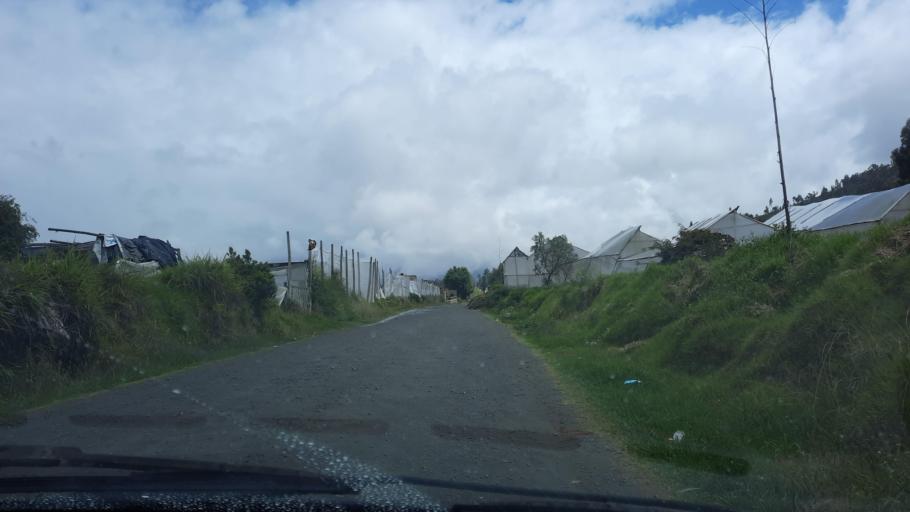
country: EC
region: Chimborazo
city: Riobamba
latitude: -1.6903
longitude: -78.6682
